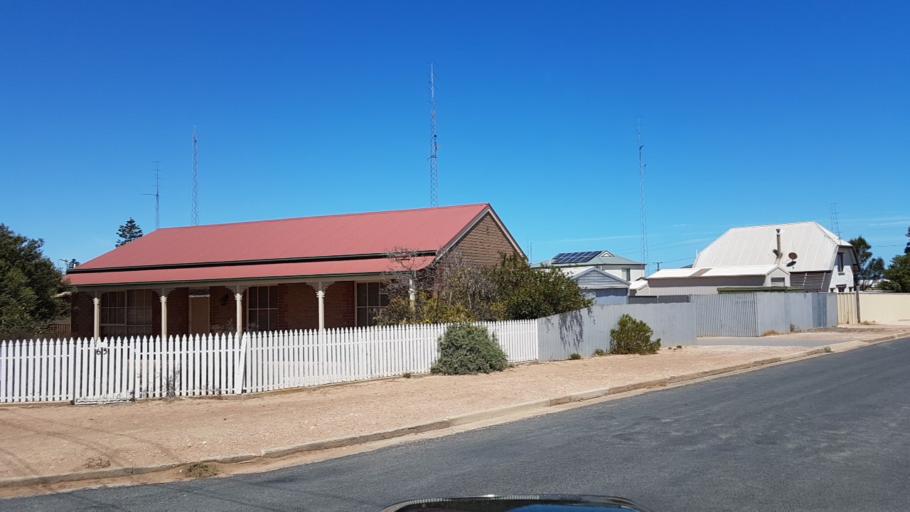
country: AU
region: South Australia
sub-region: Copper Coast
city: Wallaroo
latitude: -33.8959
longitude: 137.6297
